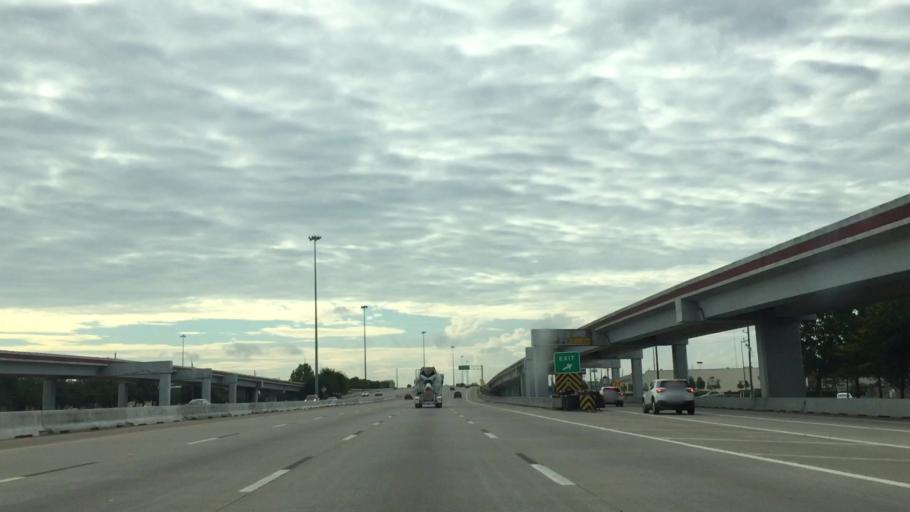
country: US
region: Texas
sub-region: Harris County
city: Jersey Village
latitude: 29.9640
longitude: -95.5518
